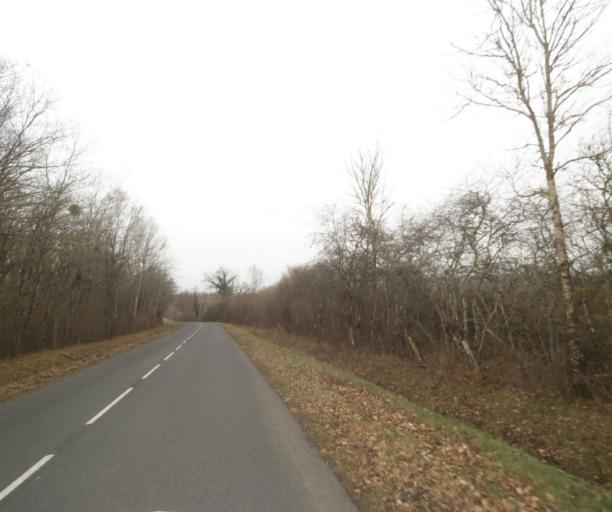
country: FR
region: Champagne-Ardenne
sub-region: Departement de la Marne
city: Pargny-sur-Saulx
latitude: 48.7373
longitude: 4.8814
